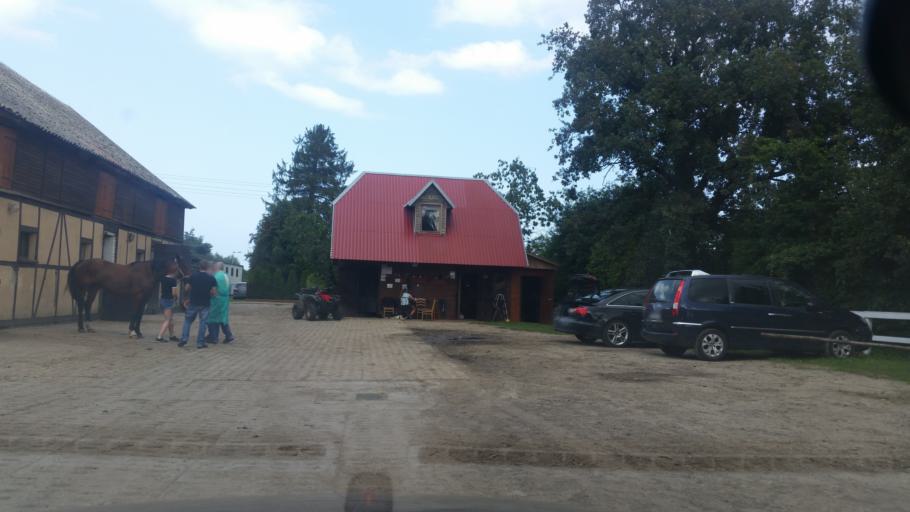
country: PL
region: Pomeranian Voivodeship
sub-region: Powiat wejherowski
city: Choczewo
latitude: 54.7693
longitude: 17.7973
